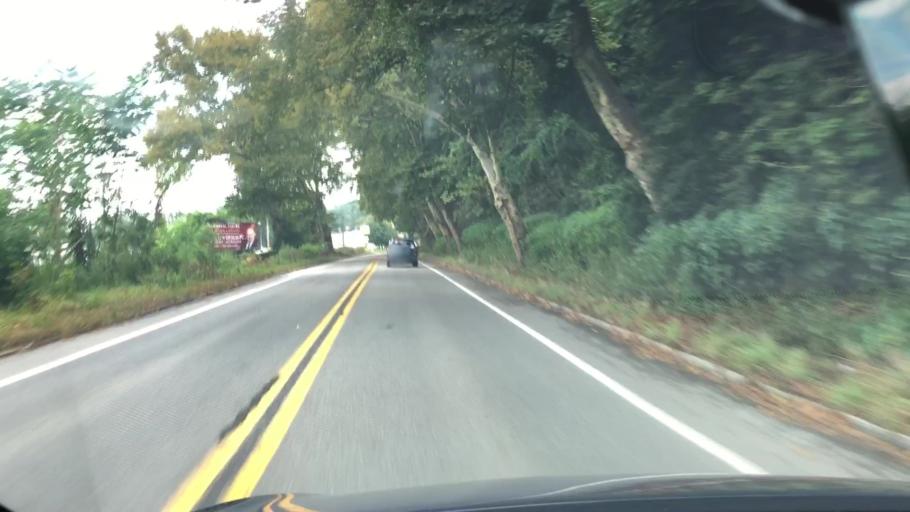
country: US
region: Pennsylvania
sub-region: Allegheny County
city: Penn Hills
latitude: 40.4931
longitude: -79.8473
